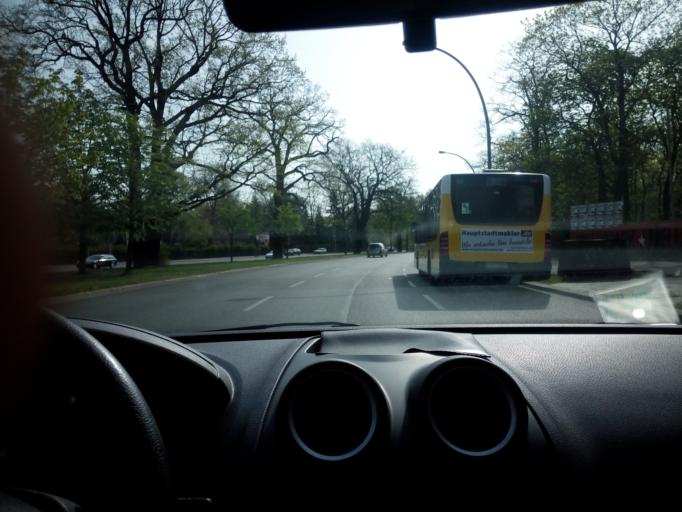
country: DE
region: Berlin
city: Kopenick Bezirk
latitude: 52.4575
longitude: 13.5619
